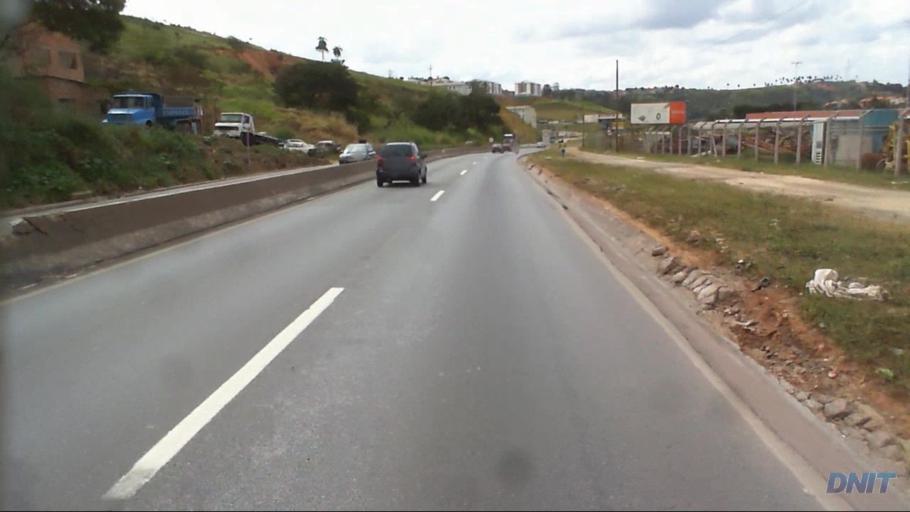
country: BR
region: Minas Gerais
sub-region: Santa Luzia
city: Santa Luzia
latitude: -19.8487
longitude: -43.8878
